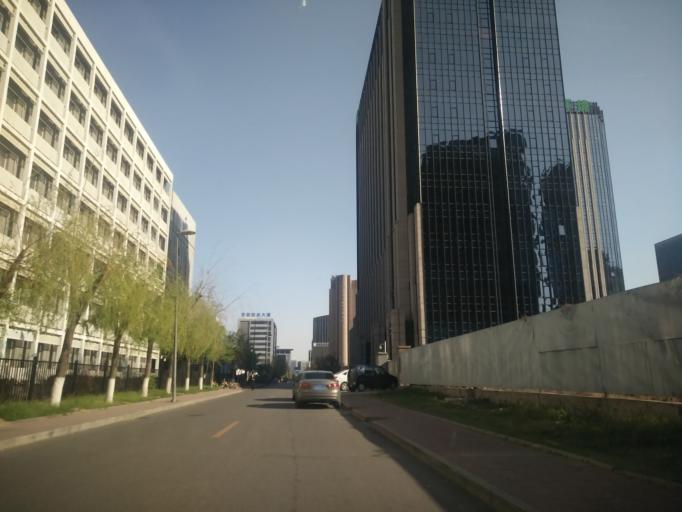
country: CN
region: Beijing
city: Jiugong
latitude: 39.7886
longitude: 116.5085
